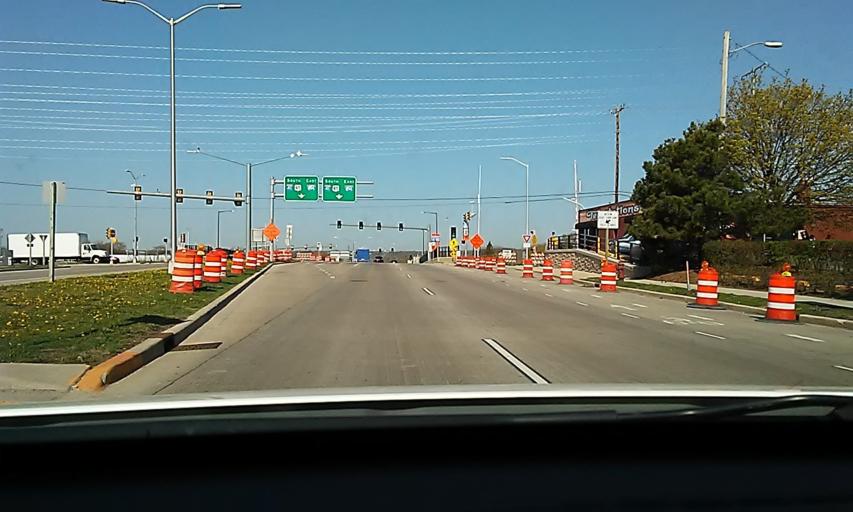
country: US
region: Wisconsin
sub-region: Milwaukee County
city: West Allis
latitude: 43.0165
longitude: -88.0344
